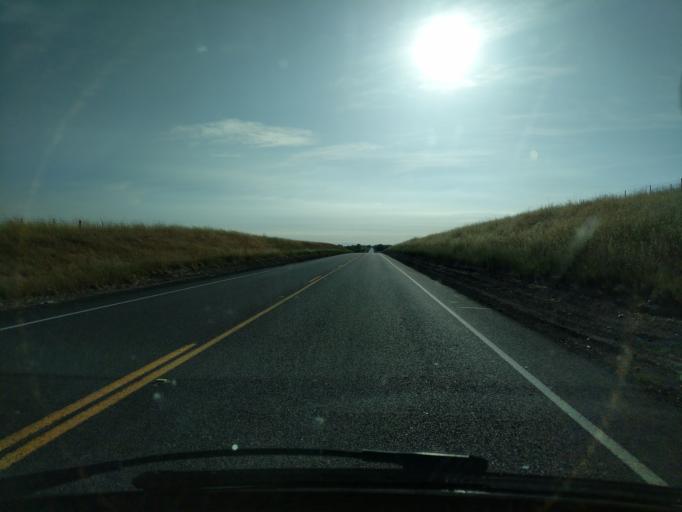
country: US
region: California
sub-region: San Joaquin County
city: Escalon
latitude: 37.9303
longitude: -120.9571
